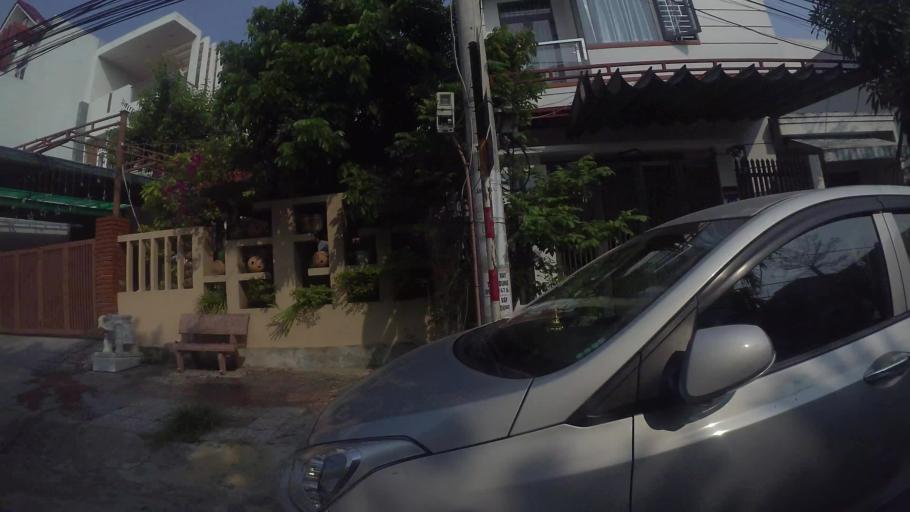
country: VN
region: Da Nang
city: Ngu Hanh Son
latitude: 16.0302
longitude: 108.2461
